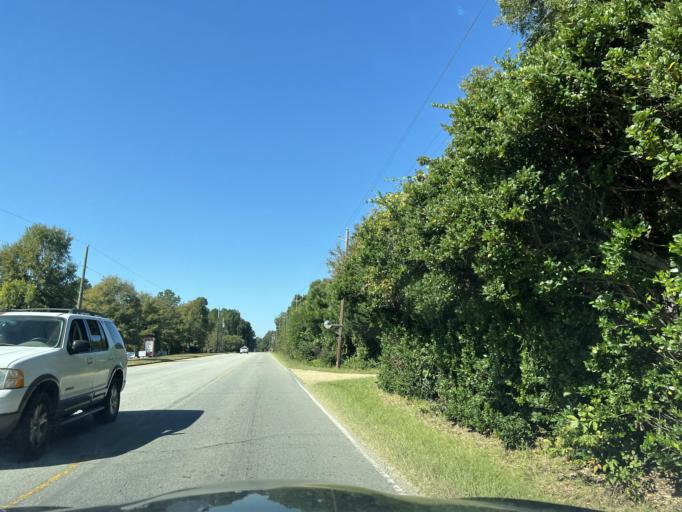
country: US
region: North Carolina
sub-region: Johnston County
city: Clayton
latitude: 35.6693
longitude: -78.4773
